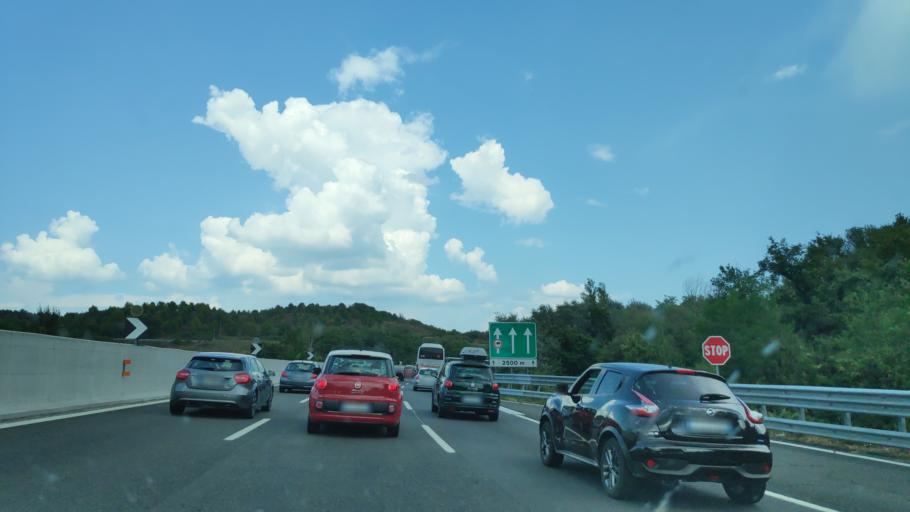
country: IT
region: Umbria
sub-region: Provincia di Terni
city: Stazione di Allerona
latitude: 42.8176
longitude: 12.0324
